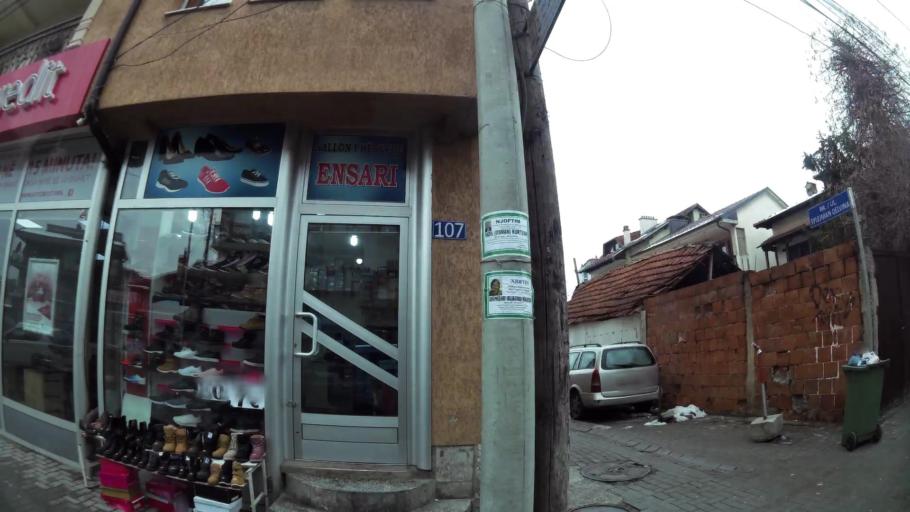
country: XK
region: Pristina
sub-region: Komuna e Prishtines
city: Pristina
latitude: 42.6695
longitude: 21.1632
